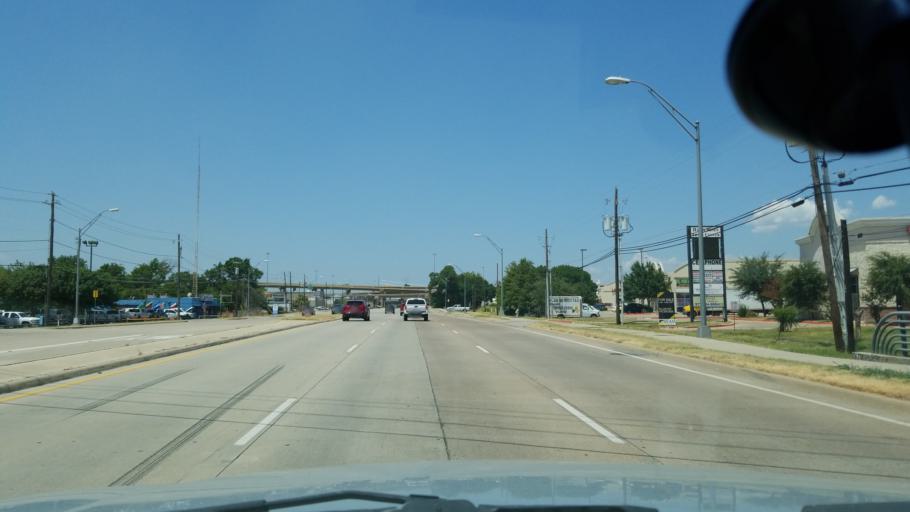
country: US
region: Texas
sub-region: Dallas County
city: Farmers Branch
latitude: 32.9015
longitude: -96.8931
